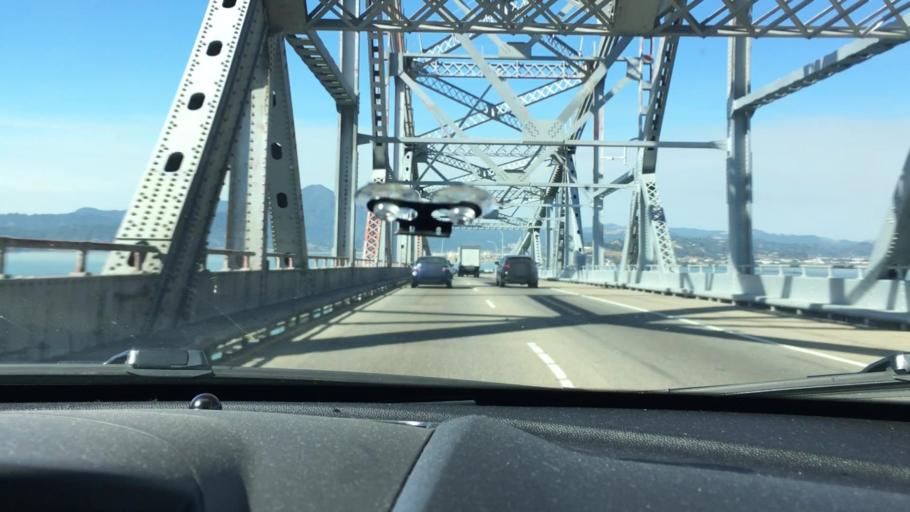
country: US
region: California
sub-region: Marin County
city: Tiburon
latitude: 37.9352
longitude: -122.4467
